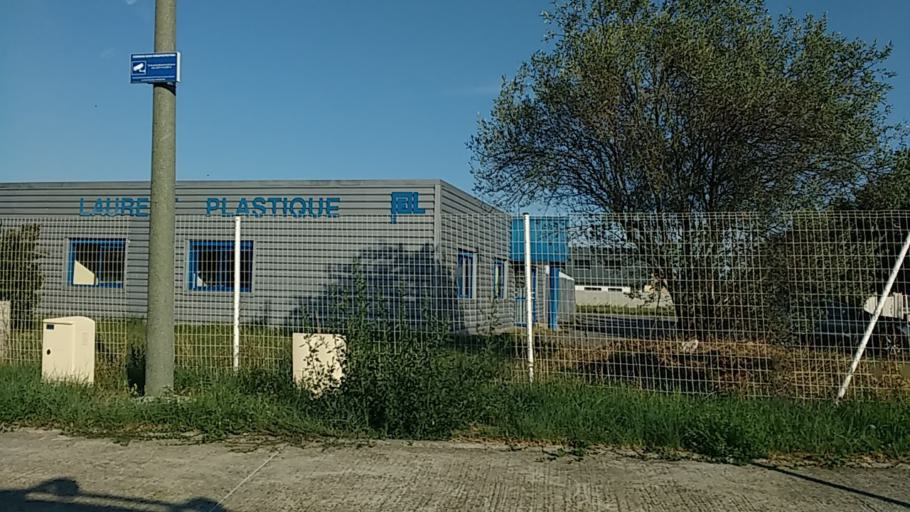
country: FR
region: Midi-Pyrenees
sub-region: Departement de la Haute-Garonne
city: Cugnaux
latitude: 43.5568
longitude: 1.3644
